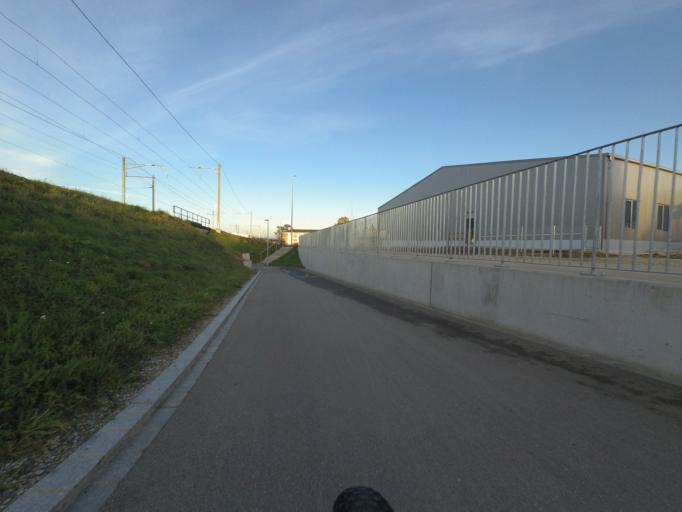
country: CH
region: Thurgau
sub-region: Frauenfeld District
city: Frauenfeld
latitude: 47.5643
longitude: 8.9062
